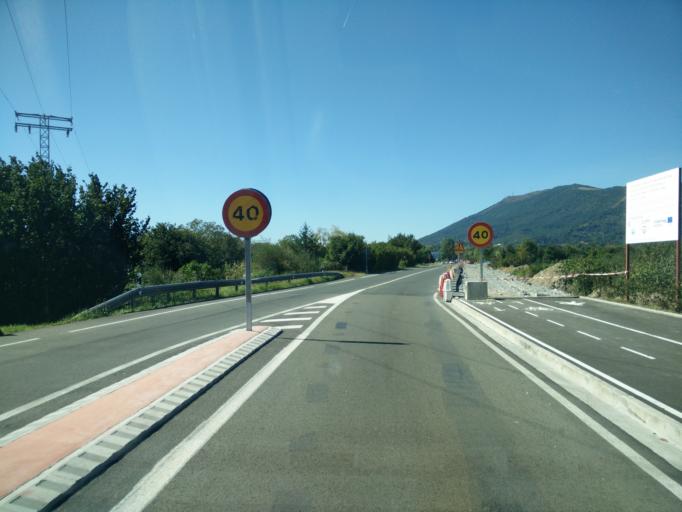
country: ES
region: Basque Country
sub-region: Provincia de Guipuzcoa
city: Irun
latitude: 43.3501
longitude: -1.8005
